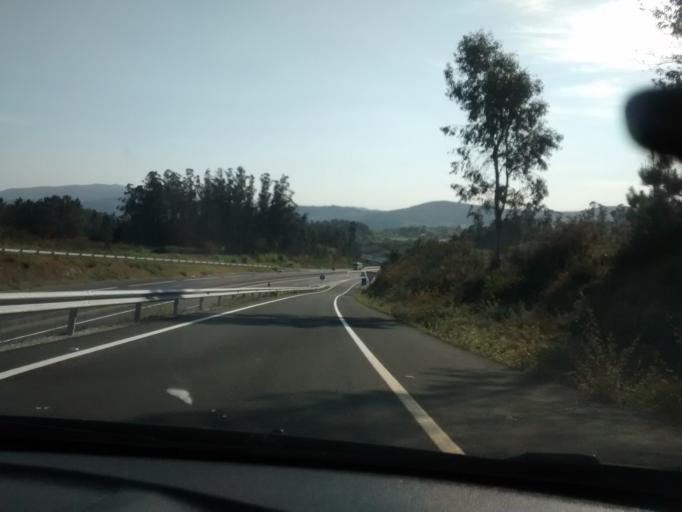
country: ES
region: Galicia
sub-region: Provincia da Coruna
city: Teo
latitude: 42.7988
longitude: -8.5360
